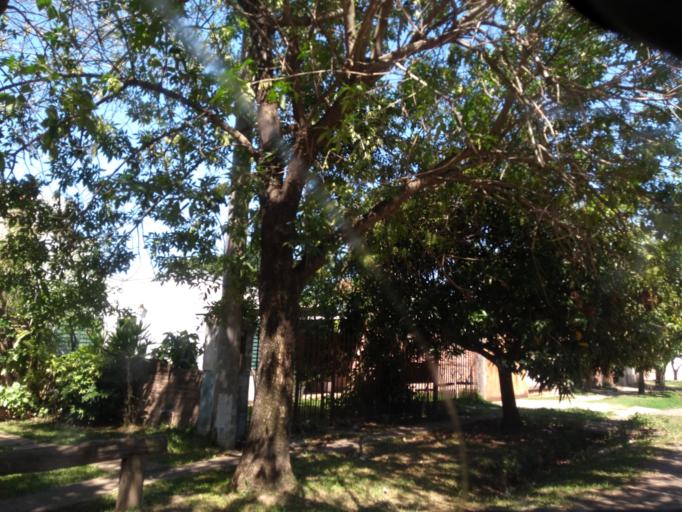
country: AR
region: Chaco
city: Fontana
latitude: -27.4112
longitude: -59.0353
